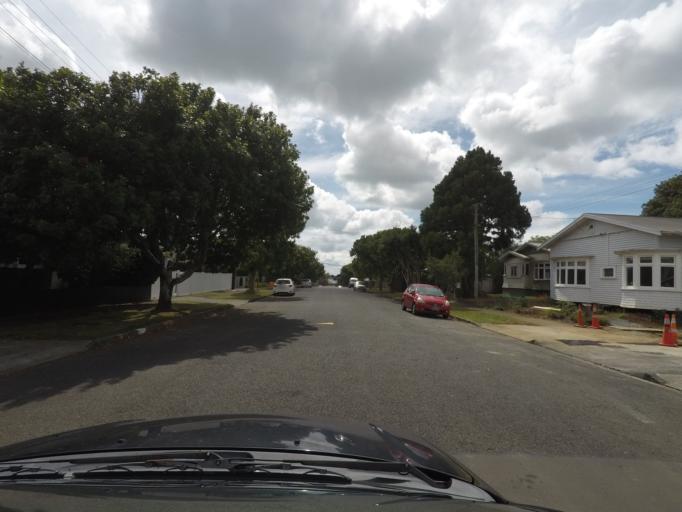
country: NZ
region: Auckland
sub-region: Auckland
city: Rosebank
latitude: -36.8843
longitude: 174.7079
